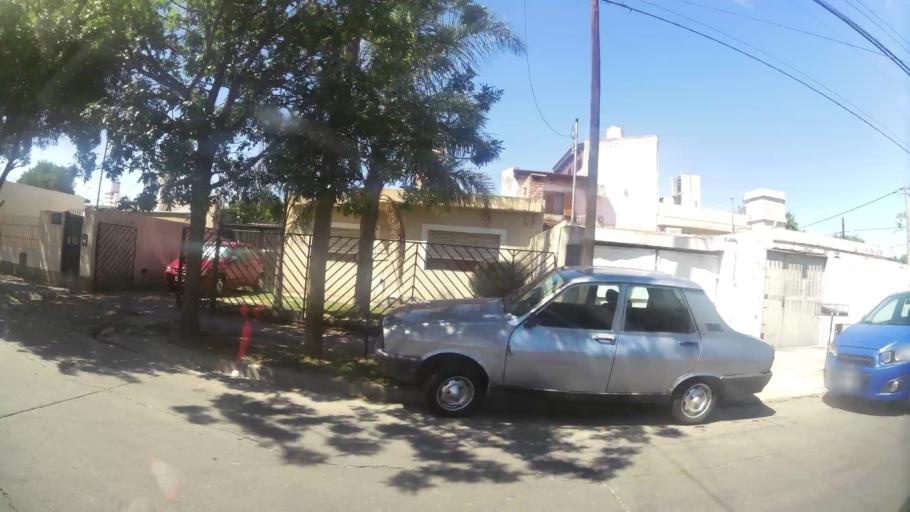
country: AR
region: Cordoba
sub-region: Departamento de Capital
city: Cordoba
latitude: -31.4203
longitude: -64.2197
